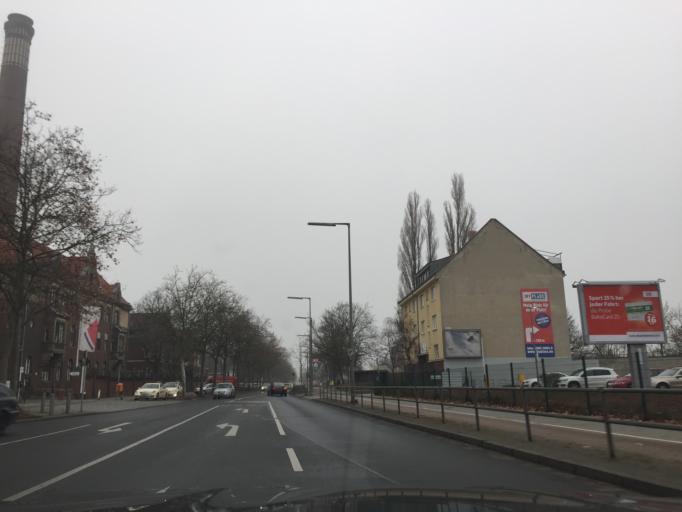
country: DE
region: Berlin
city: Charlottenburg Bezirk
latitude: 52.5199
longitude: 13.2802
